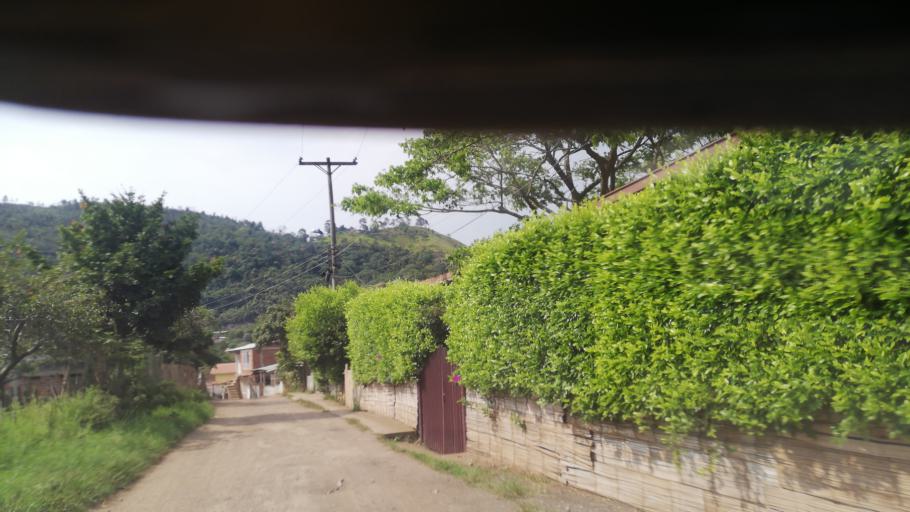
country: CO
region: Valle del Cauca
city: Cali
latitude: 3.4990
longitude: -76.5474
